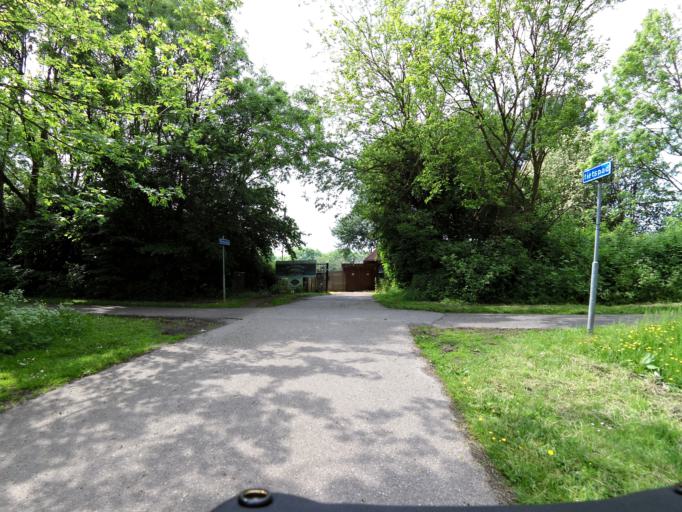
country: NL
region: South Holland
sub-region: Gemeente Maassluis
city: Maassluis
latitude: 51.8530
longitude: 4.2473
